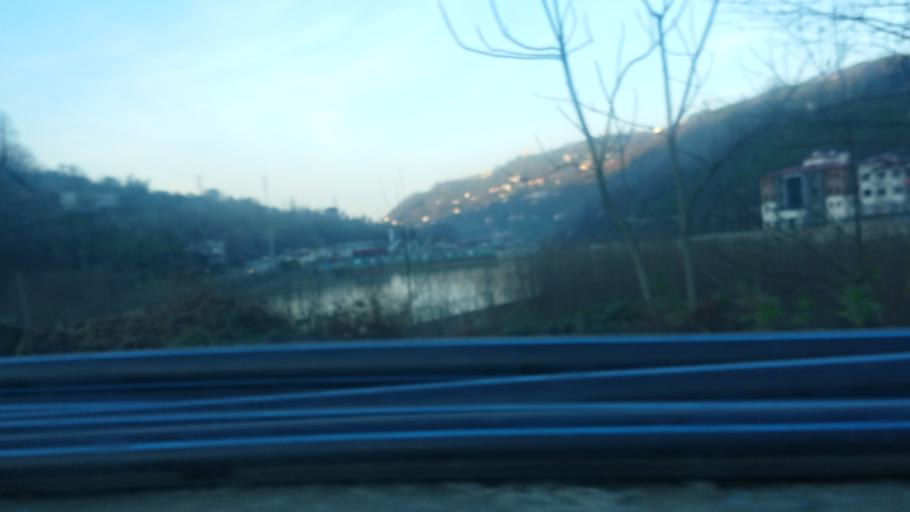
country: TR
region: Rize
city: Gundogdu
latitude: 41.0193
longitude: 40.5755
